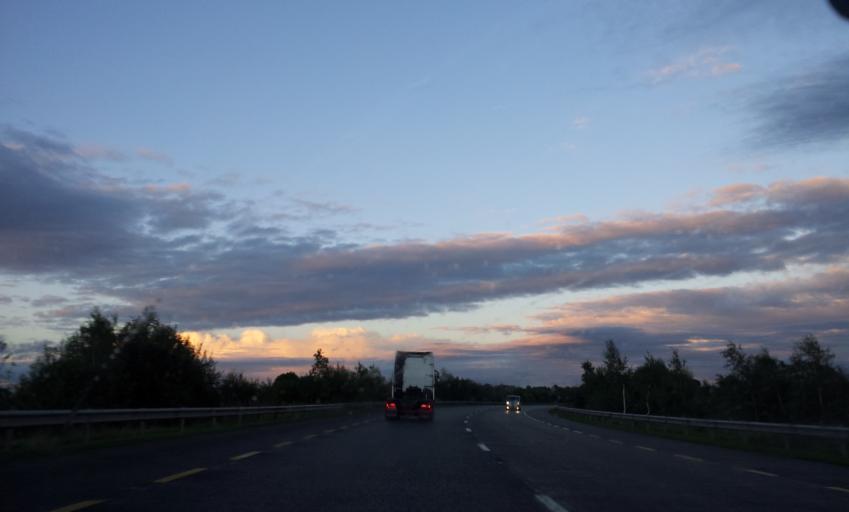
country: IE
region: Munster
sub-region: County Limerick
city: Adare
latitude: 52.5773
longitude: -8.7623
